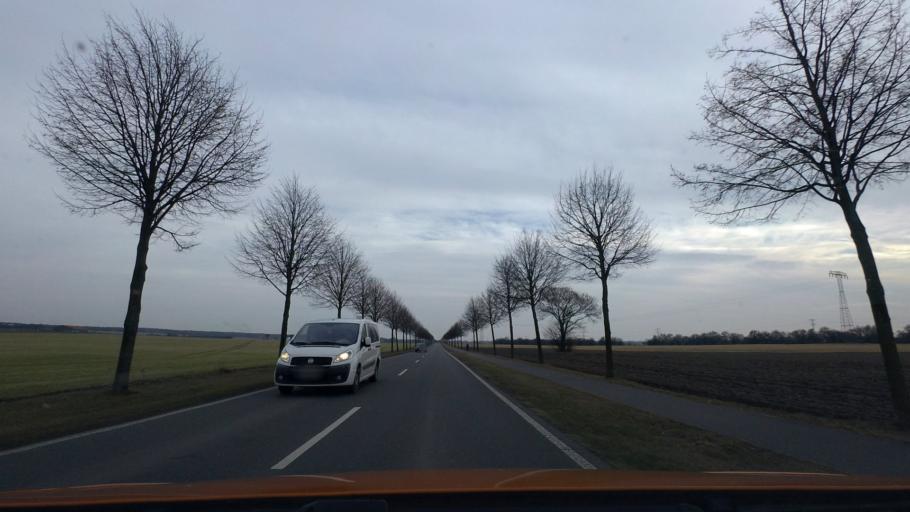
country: DE
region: Berlin
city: Falkenberg
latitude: 52.5963
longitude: 13.5411
